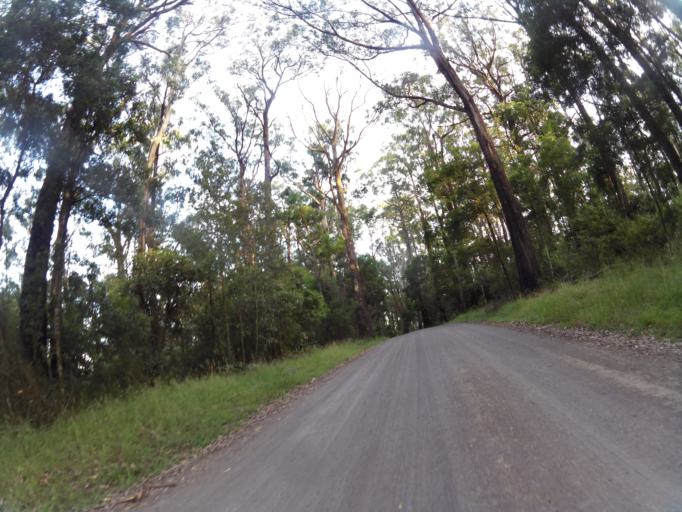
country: AU
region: Victoria
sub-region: Colac-Otway
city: Apollo Bay
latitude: -38.5512
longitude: 143.7376
